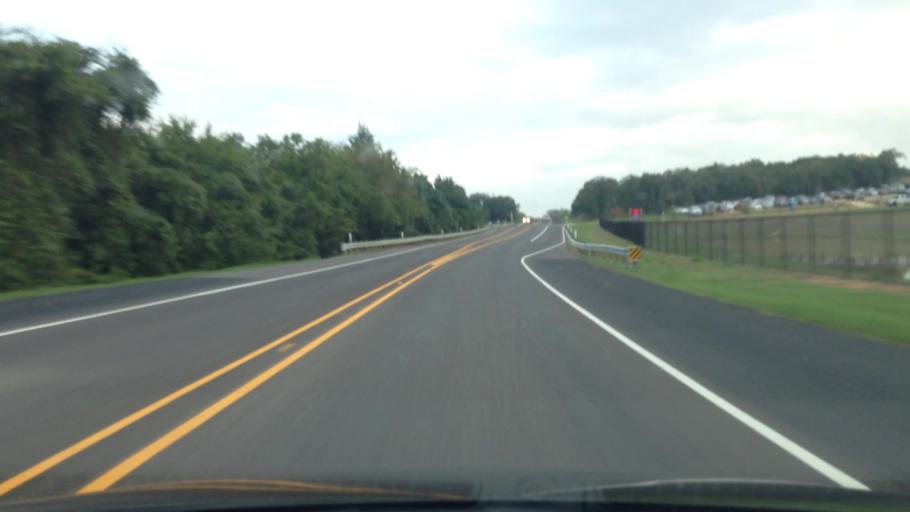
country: US
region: Texas
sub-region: Johnson County
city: Joshua
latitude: 32.4820
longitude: -97.3392
